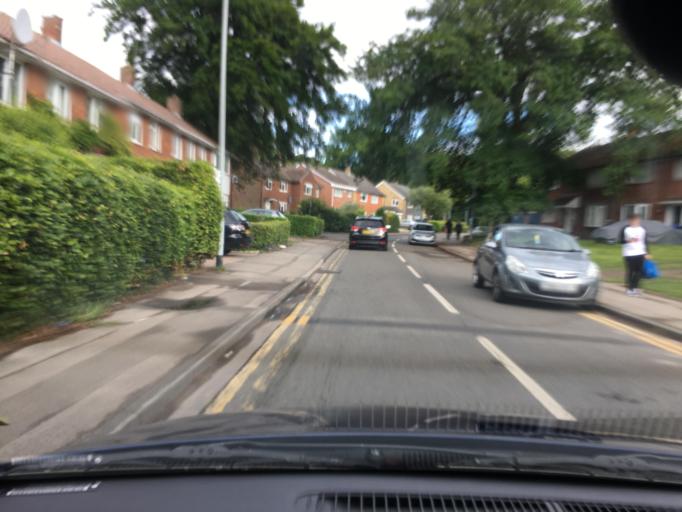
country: GB
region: England
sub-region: Bracknell Forest
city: Bracknell
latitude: 51.3998
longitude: -0.7537
